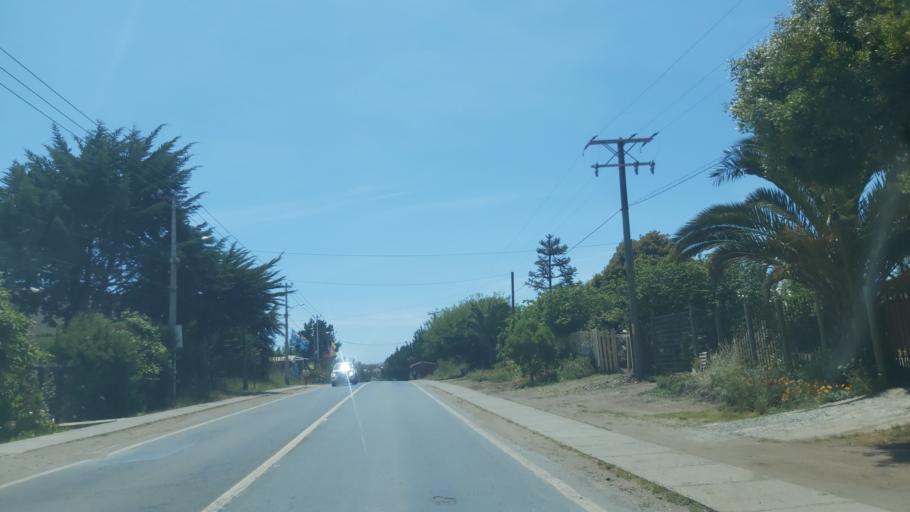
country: CL
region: Maule
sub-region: Provincia de Cauquenes
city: Cauquenes
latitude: -35.8022
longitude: -72.5656
